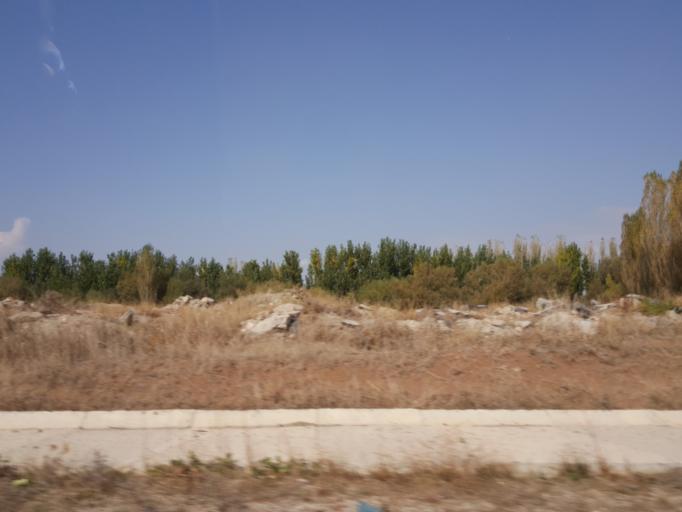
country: TR
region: Corum
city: Alaca
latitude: 40.1547
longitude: 34.8581
